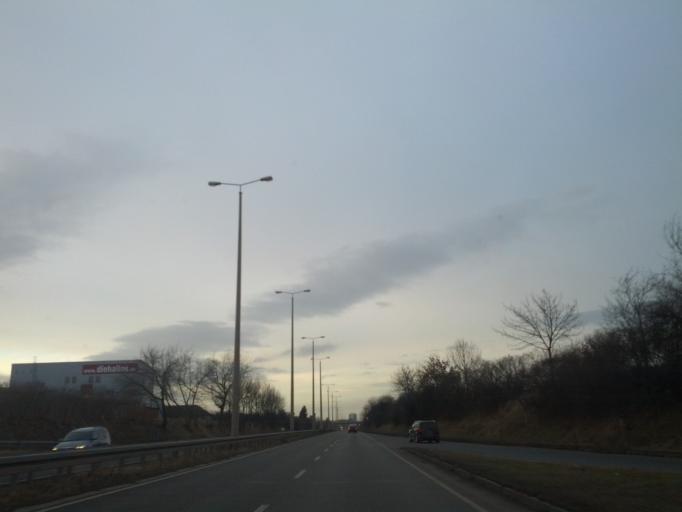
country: DE
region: Thuringia
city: Erfurt
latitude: 50.9856
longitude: 11.0060
